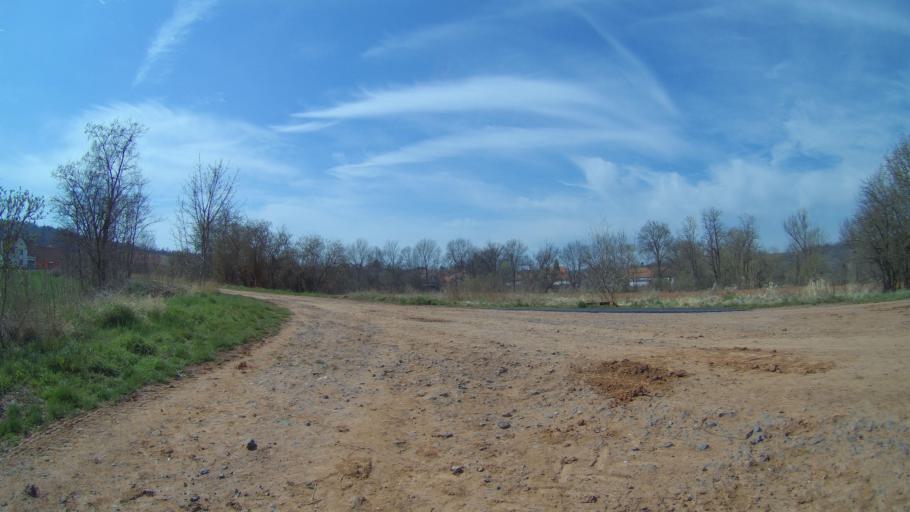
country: CZ
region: Ustecky
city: Podborany
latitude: 50.2193
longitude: 13.4763
